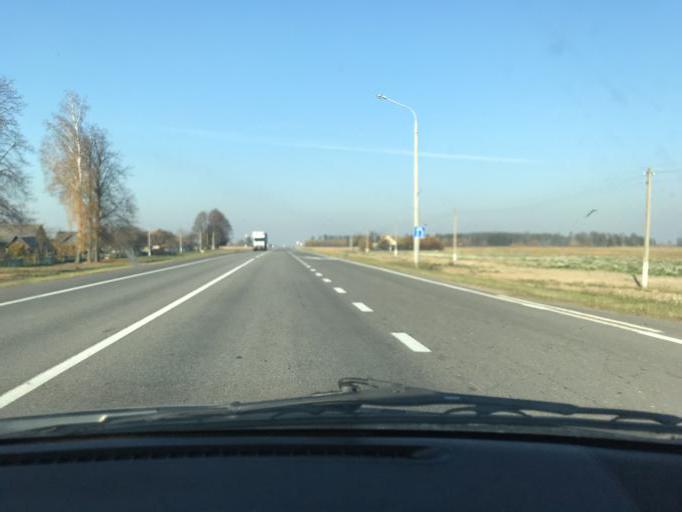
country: BY
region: Vitebsk
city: Orsha
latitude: 54.3380
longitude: 30.4462
